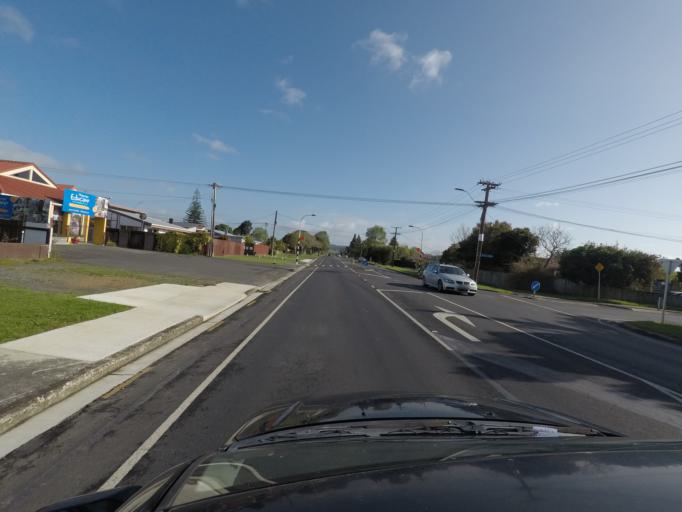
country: NZ
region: Northland
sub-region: Whangarei
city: Whangarei
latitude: -35.6913
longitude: 174.3271
